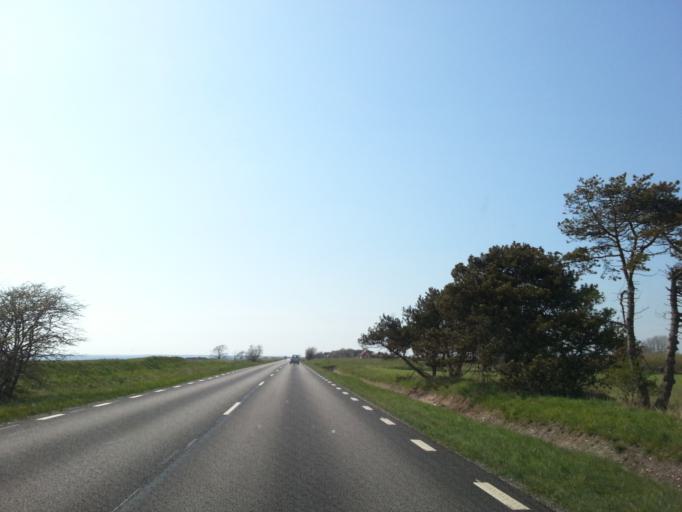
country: SE
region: Skane
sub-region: Trelleborgs Kommun
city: Skare
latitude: 55.3788
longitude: 13.0453
